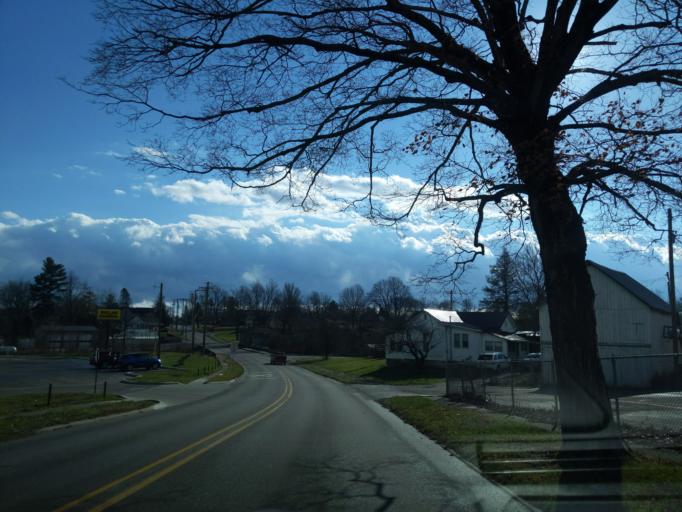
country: US
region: Indiana
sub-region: Decatur County
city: Greensburg
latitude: 39.3353
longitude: -85.4802
